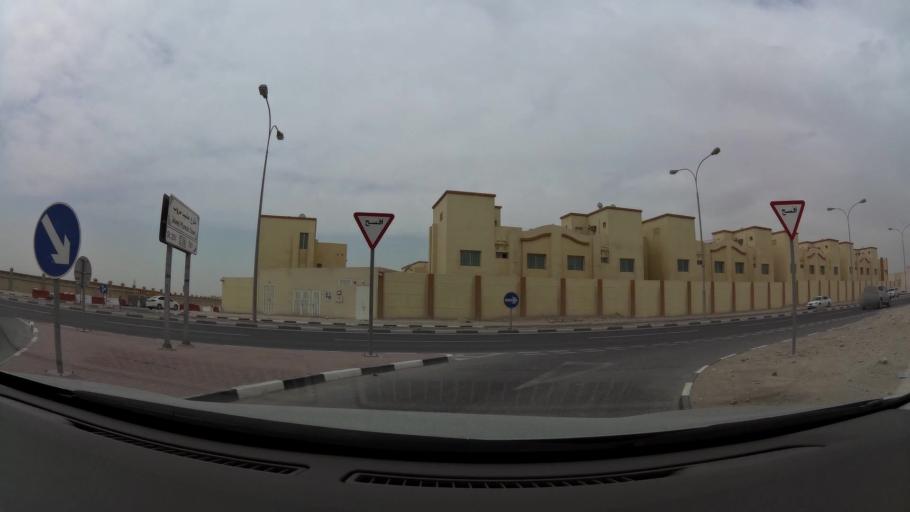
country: QA
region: Baladiyat ar Rayyan
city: Ar Rayyan
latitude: 25.2291
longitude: 51.4482
